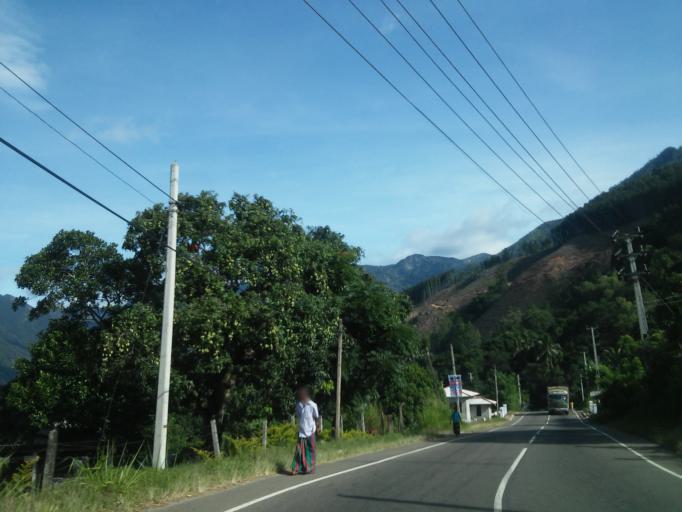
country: LK
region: Uva
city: Haputale
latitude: 6.7609
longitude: 80.8762
